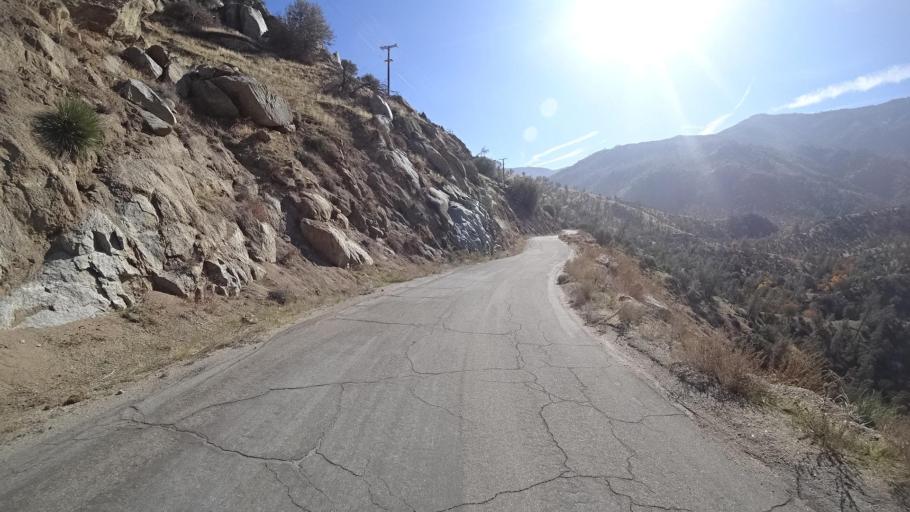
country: US
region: California
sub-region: Kern County
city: Bodfish
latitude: 35.5426
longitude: -118.6146
